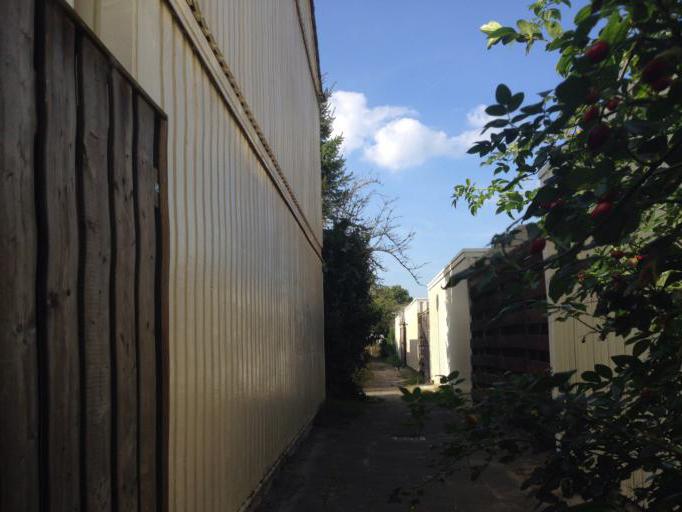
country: NL
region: Flevoland
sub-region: Gemeente Almere
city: Almere Stad
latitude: 52.3969
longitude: 5.2618
